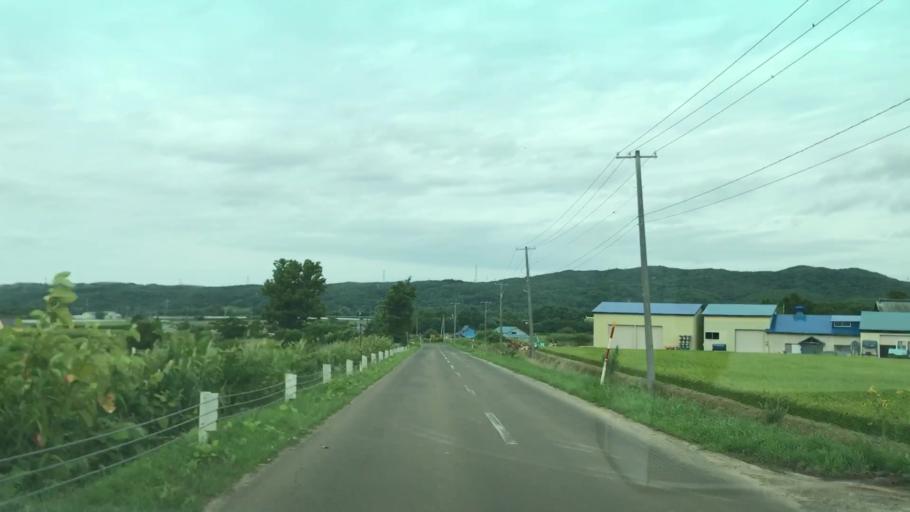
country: JP
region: Hokkaido
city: Iwanai
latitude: 43.0341
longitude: 140.5635
